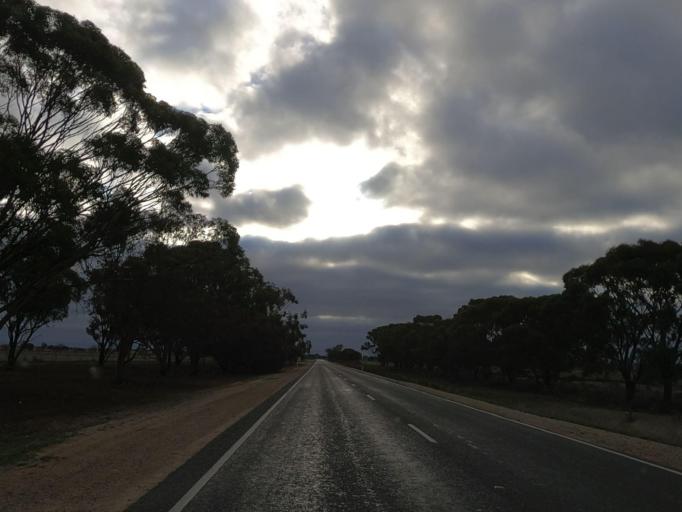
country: AU
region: Victoria
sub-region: Swan Hill
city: Swan Hill
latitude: -35.6570
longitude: 143.8524
